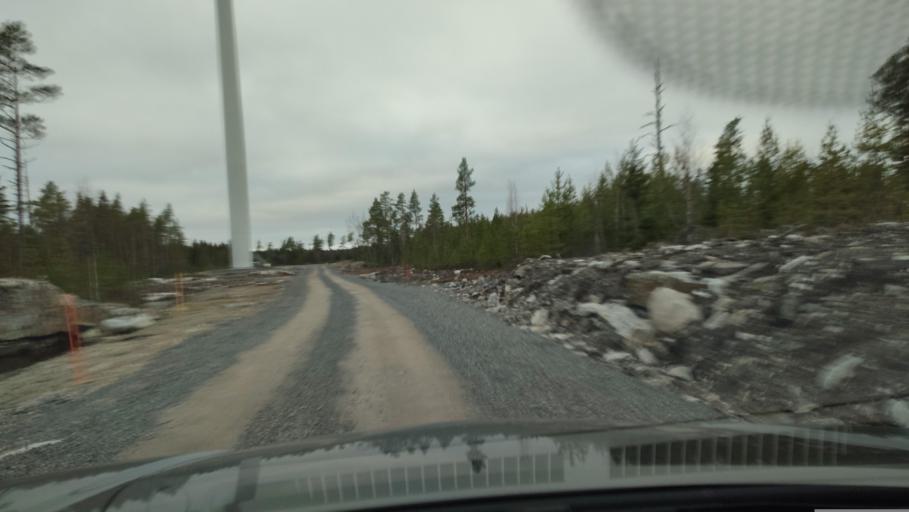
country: FI
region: Southern Ostrobothnia
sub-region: Suupohja
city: Karijoki
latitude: 62.2003
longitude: 21.5516
